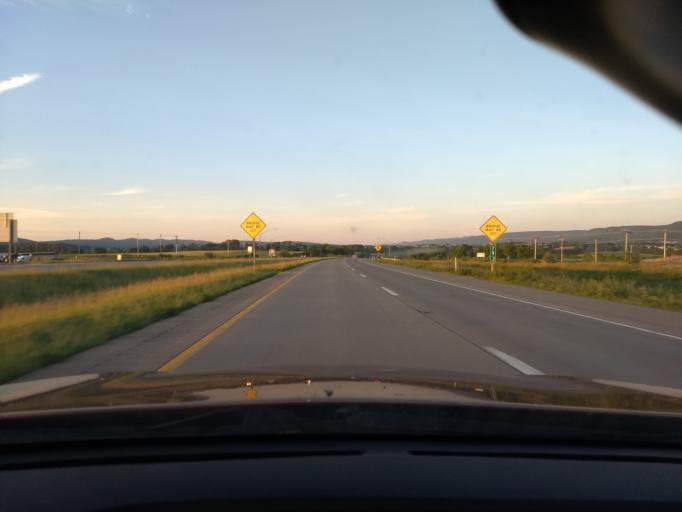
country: US
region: Pennsylvania
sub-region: Centre County
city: Pleasant Gap
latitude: 40.8739
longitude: -77.7768
